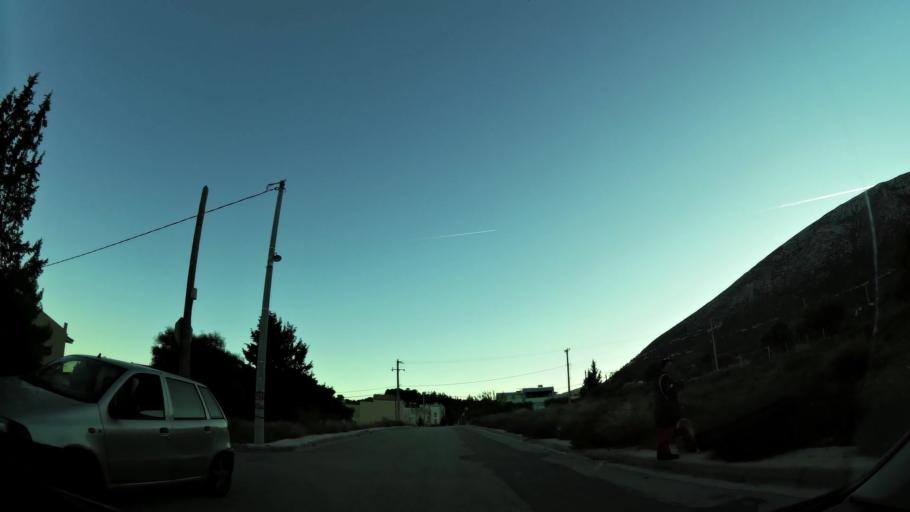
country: GR
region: Attica
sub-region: Nomarchia Anatolikis Attikis
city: Paiania
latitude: 37.9565
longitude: 23.8447
